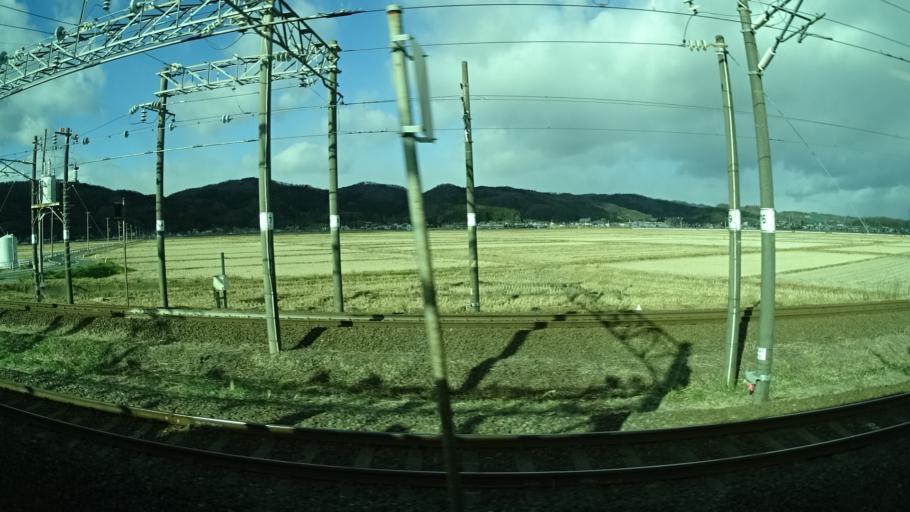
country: JP
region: Miyagi
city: Iwanuma
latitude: 38.0991
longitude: 140.8530
